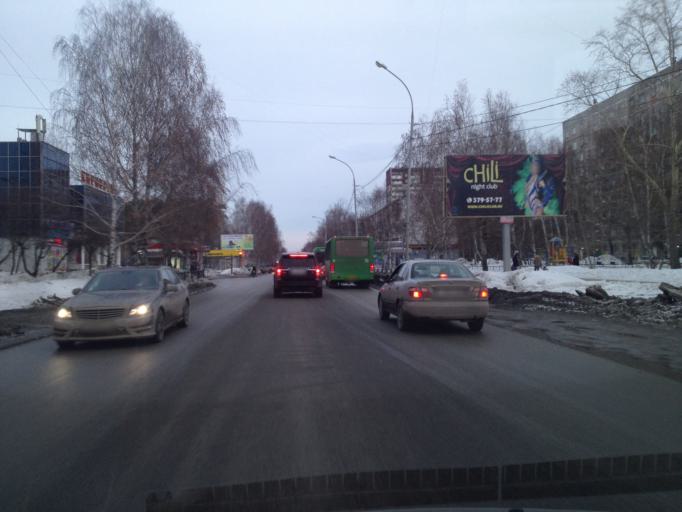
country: RU
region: Sverdlovsk
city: Sovkhoznyy
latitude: 56.8068
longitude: 60.5550
